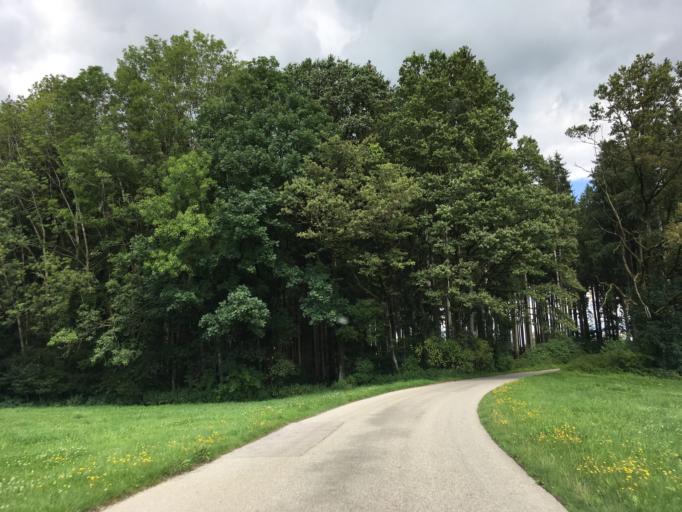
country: DE
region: Bavaria
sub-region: Upper Bavaria
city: Pittenhart
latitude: 48.0096
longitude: 12.3660
